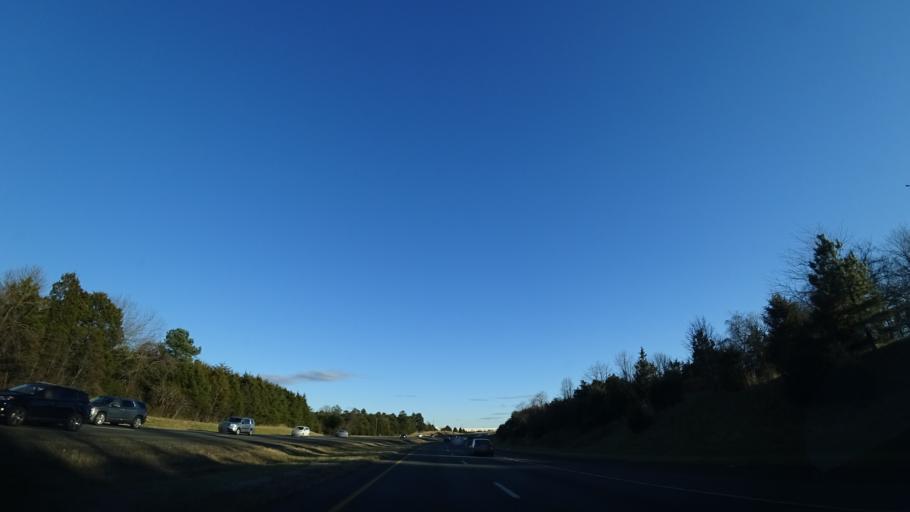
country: US
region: Virginia
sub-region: Prince William County
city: Bull Run
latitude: 38.7910
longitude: -77.5557
